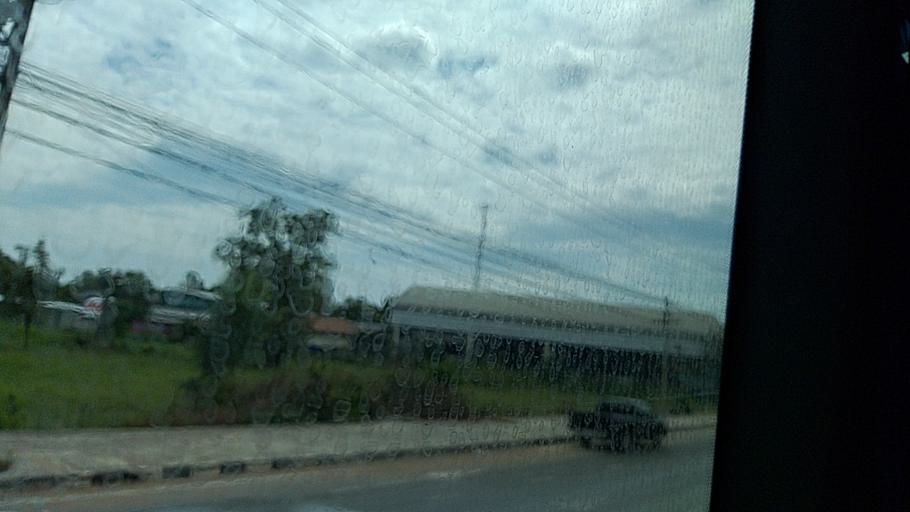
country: TH
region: Maha Sarakham
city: Maha Sarakham
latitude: 16.2439
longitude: 103.2721
